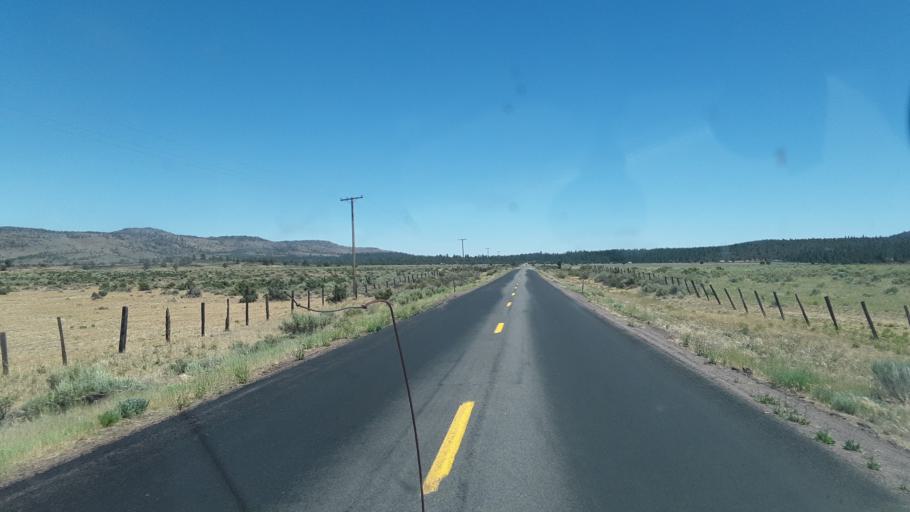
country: US
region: California
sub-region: Lassen County
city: Susanville
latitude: 40.5324
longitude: -120.6069
